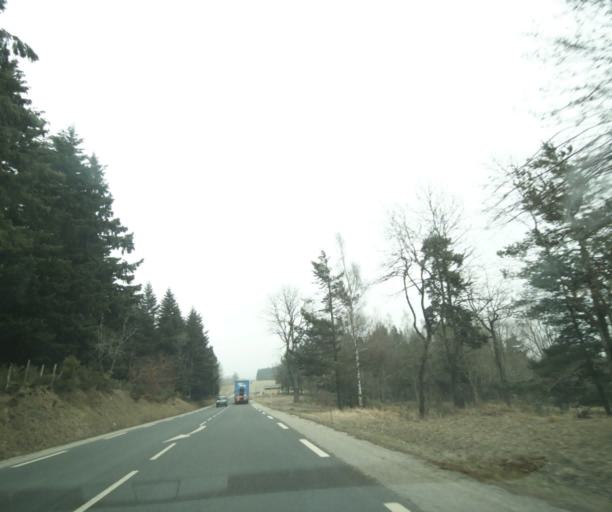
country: FR
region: Languedoc-Roussillon
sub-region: Departement de la Lozere
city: Langogne
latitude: 44.7002
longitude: 3.8175
